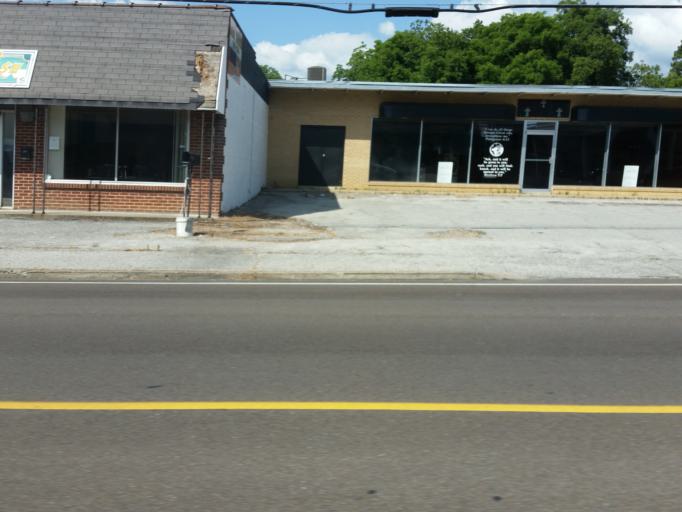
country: US
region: Tennessee
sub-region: Henderson County
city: Lexington
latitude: 35.6520
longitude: -88.3948
